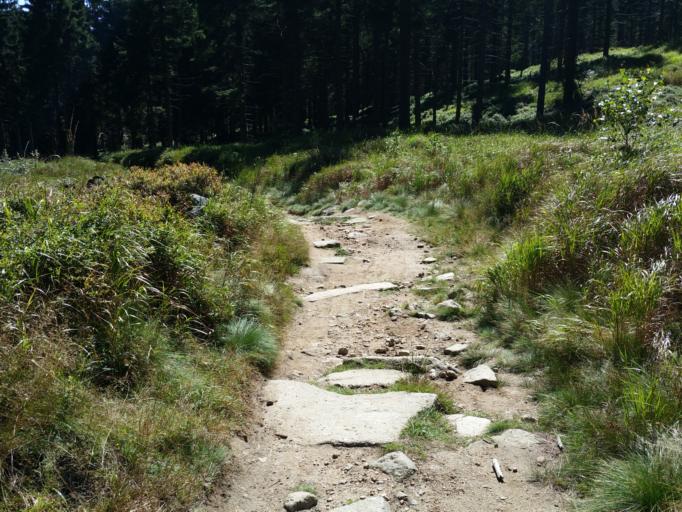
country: DE
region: Bavaria
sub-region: Upper Franconia
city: Bischofsgrun
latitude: 50.0303
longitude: 11.8161
